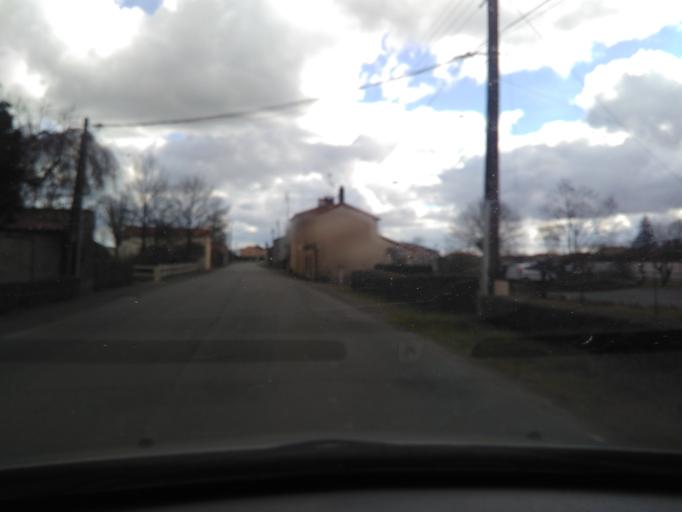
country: FR
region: Pays de la Loire
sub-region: Departement de la Vendee
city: Saint-Martin-des-Noyers
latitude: 46.7291
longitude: -1.1814
